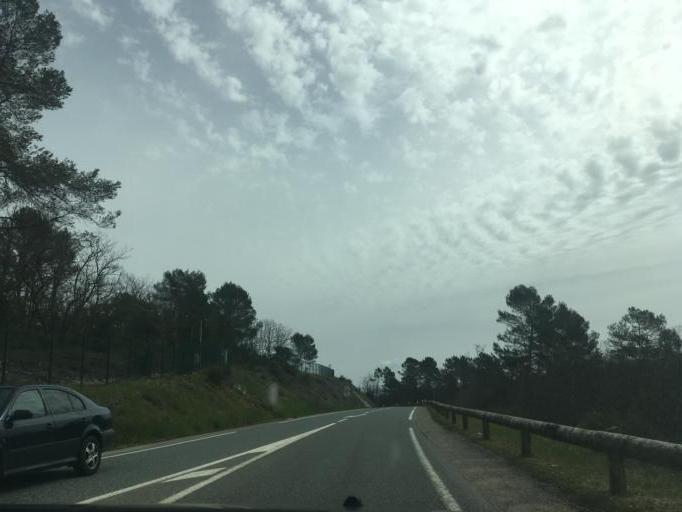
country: FR
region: Provence-Alpes-Cote d'Azur
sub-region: Departement du Var
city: Callian
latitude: 43.5905
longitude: 6.7328
